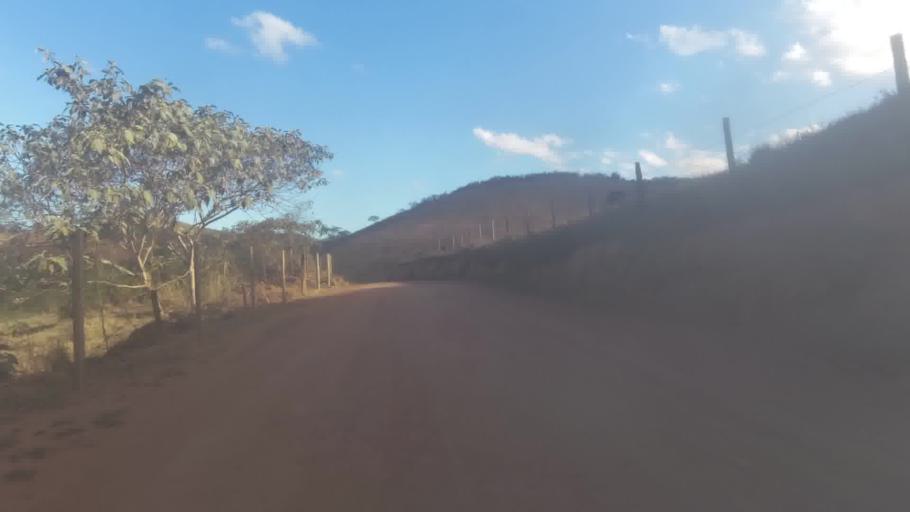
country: BR
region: Espirito Santo
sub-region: Mimoso Do Sul
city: Mimoso do Sul
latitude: -21.0773
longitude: -41.1458
